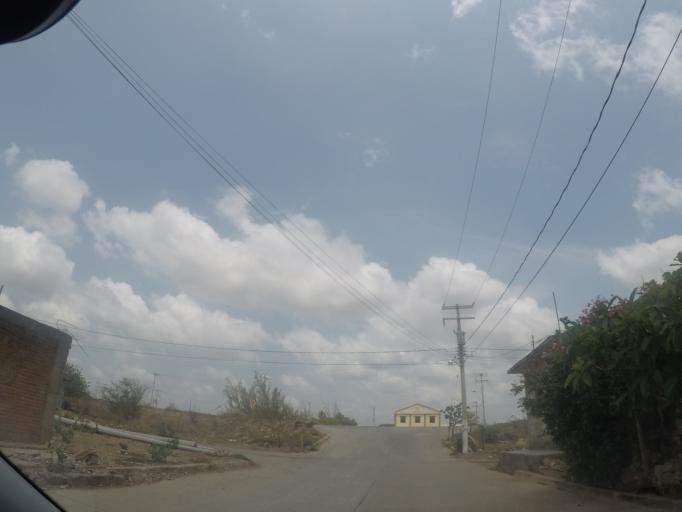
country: MX
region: Oaxaca
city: El Espinal
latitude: 16.5552
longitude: -94.9485
